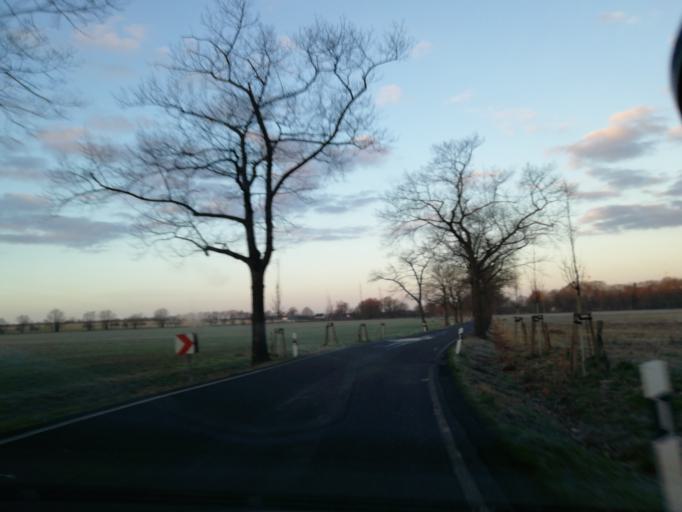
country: DE
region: Brandenburg
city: Calau
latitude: 51.7367
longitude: 13.9214
